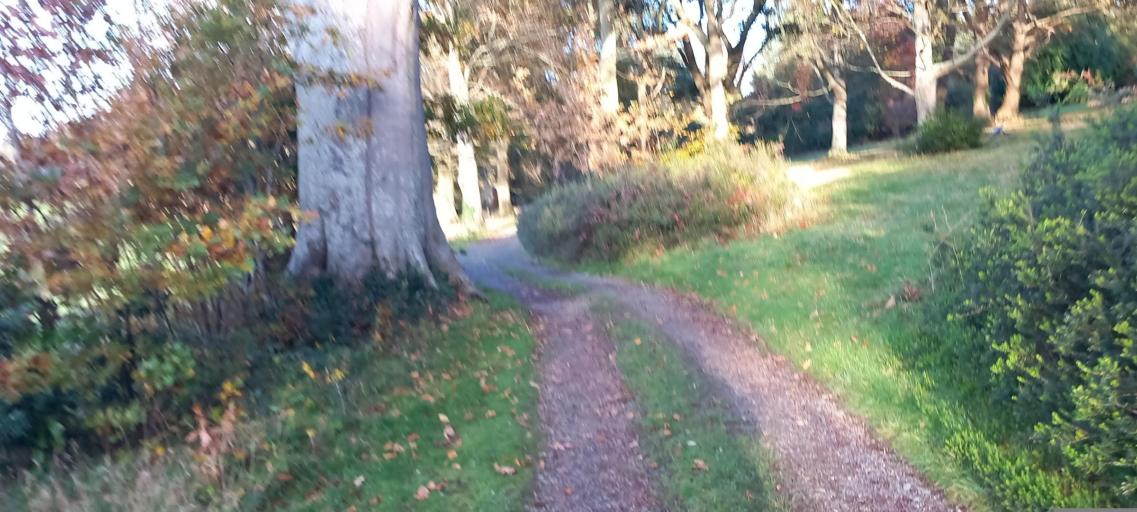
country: GB
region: Wales
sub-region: Gwynedd
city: Bangor
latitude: 53.2241
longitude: -4.0961
